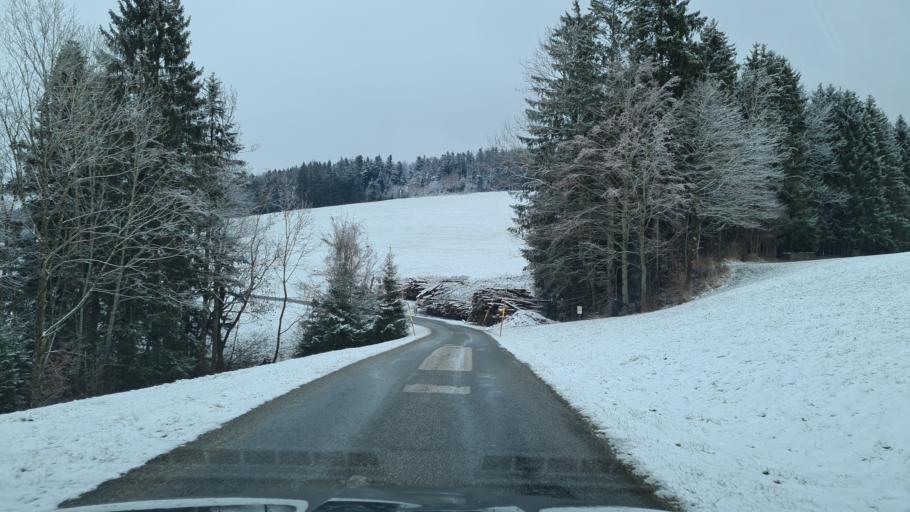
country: AT
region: Upper Austria
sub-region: Politischer Bezirk Vocklabruck
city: Oberhofen am Irrsee
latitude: 47.9394
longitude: 13.3226
